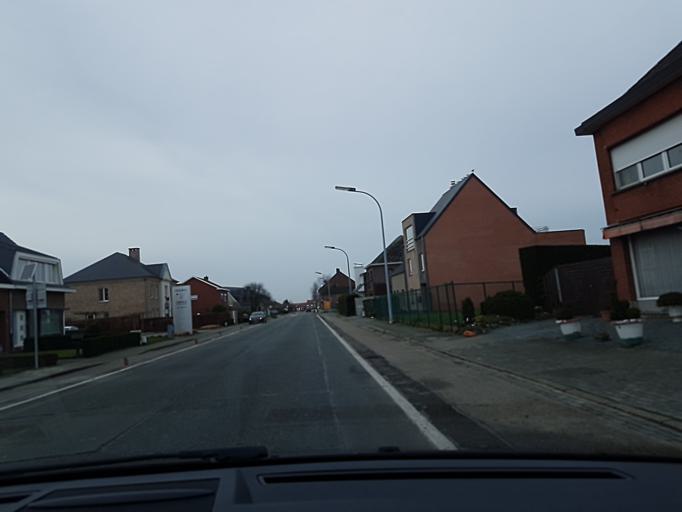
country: BE
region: Flanders
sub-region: Provincie Antwerpen
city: Putte
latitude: 51.0601
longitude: 4.6210
